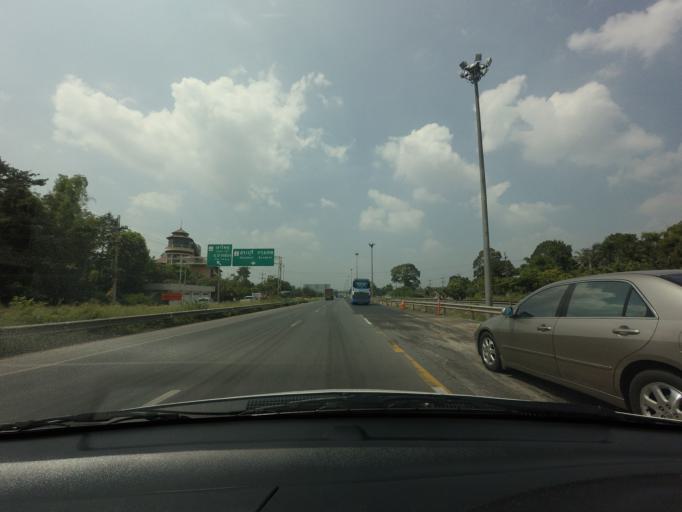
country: TH
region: Nakhon Ratchasima
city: Pak Chong
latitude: 14.6629
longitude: 101.4089
